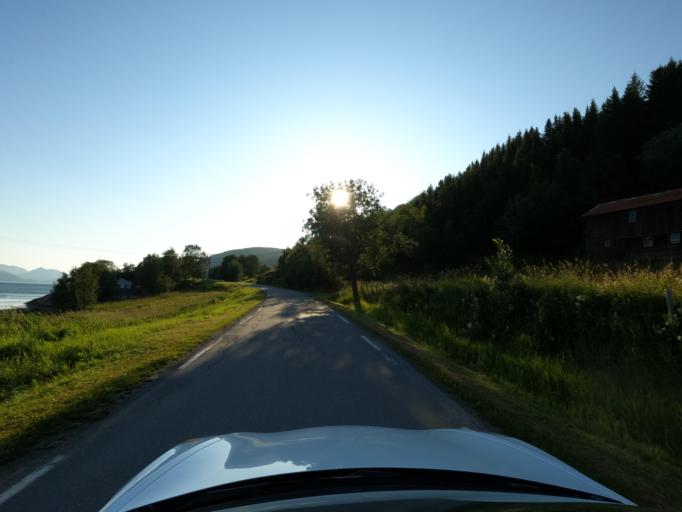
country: NO
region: Nordland
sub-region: Ballangen
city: Ballangen
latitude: 68.4684
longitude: 16.8081
